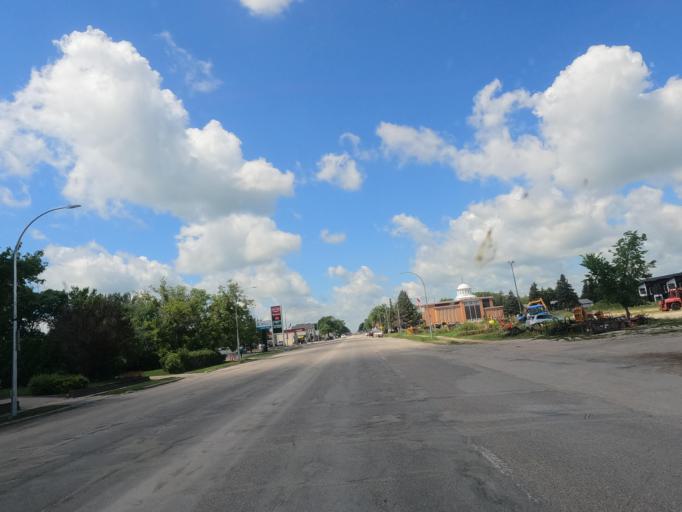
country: CA
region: Manitoba
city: Beausejour
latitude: 50.0618
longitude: -96.5059
